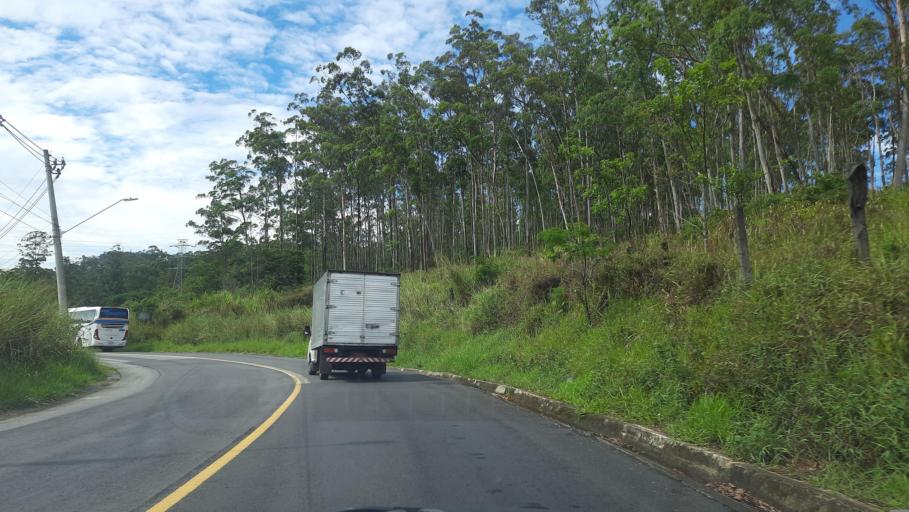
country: BR
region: Sao Paulo
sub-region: Caieiras
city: Caieiras
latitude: -23.3672
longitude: -46.6701
